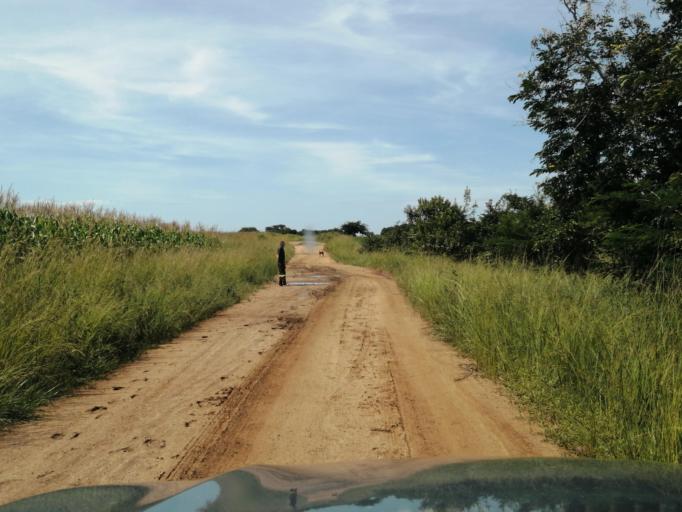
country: ZM
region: Central
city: Chibombo
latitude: -14.9747
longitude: 27.8057
